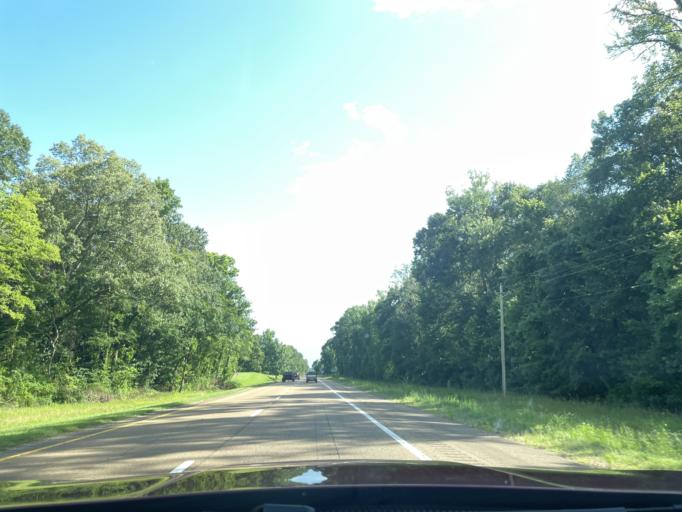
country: US
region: Mississippi
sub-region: Madison County
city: Flora
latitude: 32.4722
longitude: -90.2888
